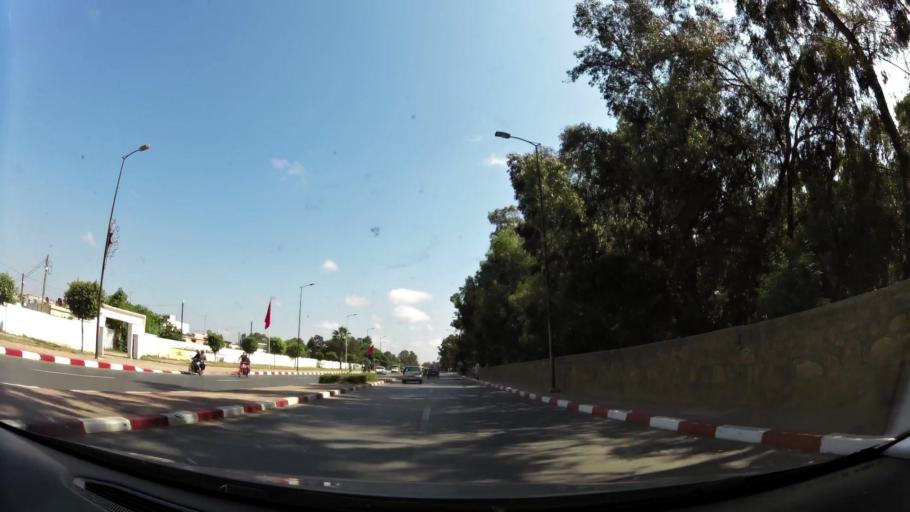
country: MA
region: Rabat-Sale-Zemmour-Zaer
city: Sale
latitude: 34.0389
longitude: -6.7752
